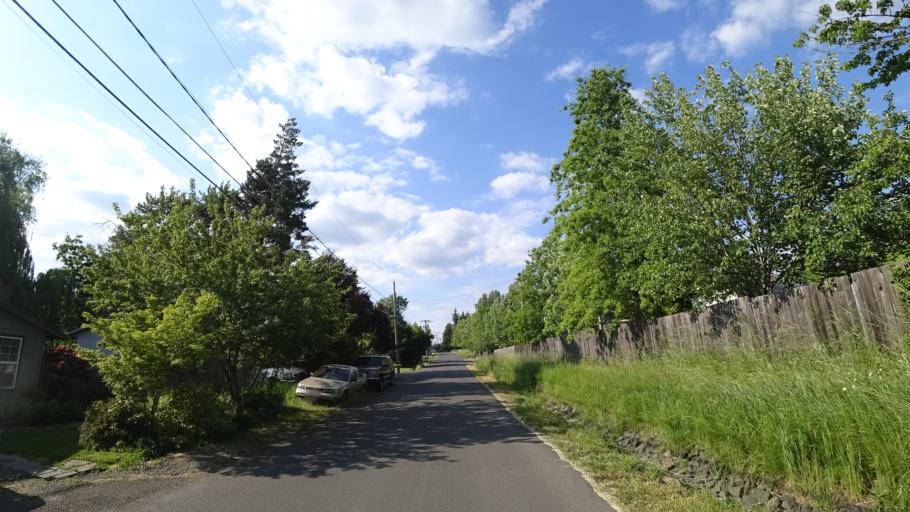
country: US
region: Oregon
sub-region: Washington County
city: Garden Home-Whitford
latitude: 45.4633
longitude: -122.7482
